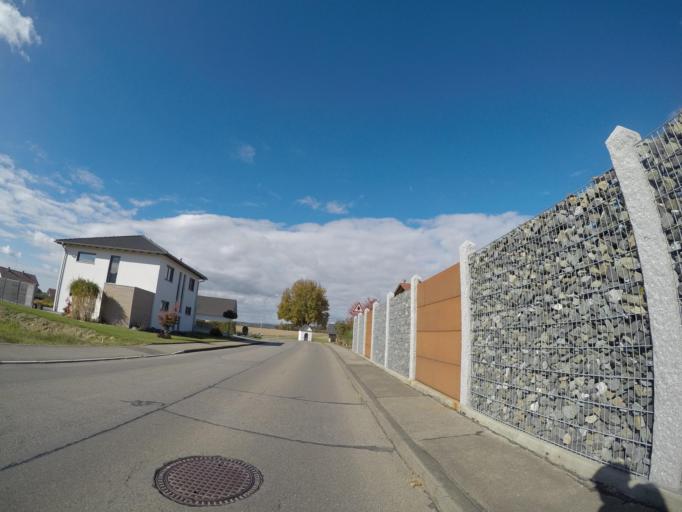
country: DE
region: Baden-Wuerttemberg
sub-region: Tuebingen Region
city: Grundsheim
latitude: 48.1514
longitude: 9.6682
